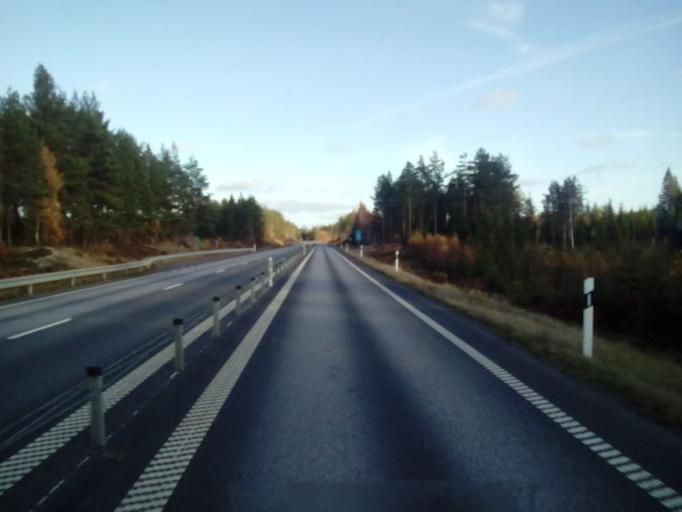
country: SE
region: Kalmar
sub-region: Vimmerby Kommun
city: Vimmerby
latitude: 57.6812
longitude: 15.9683
